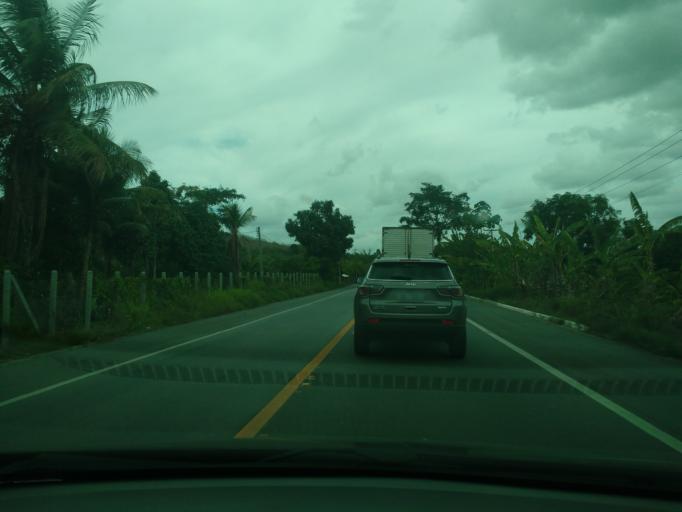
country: BR
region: Alagoas
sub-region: Uniao Dos Palmares
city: Uniao dos Palmares
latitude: -9.2326
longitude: -36.0239
